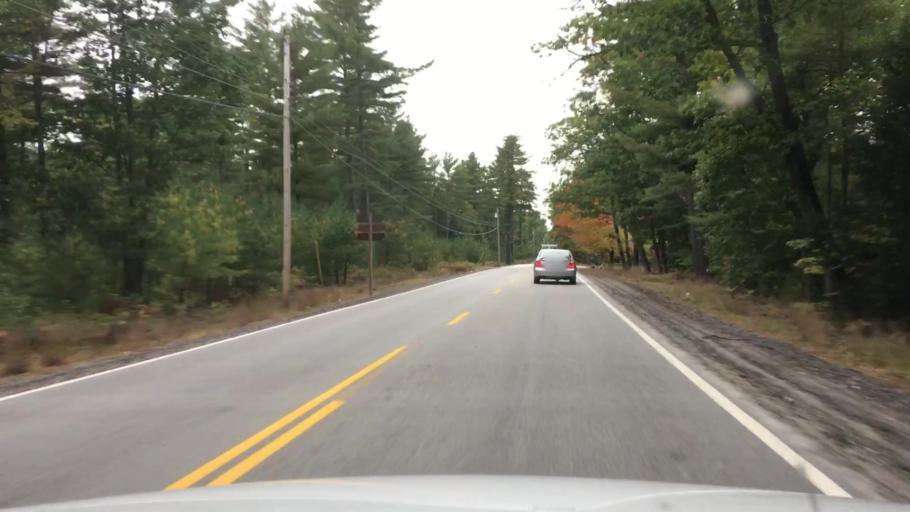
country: US
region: Maine
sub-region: Cumberland County
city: Harrison
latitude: 44.2145
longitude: -70.6833
